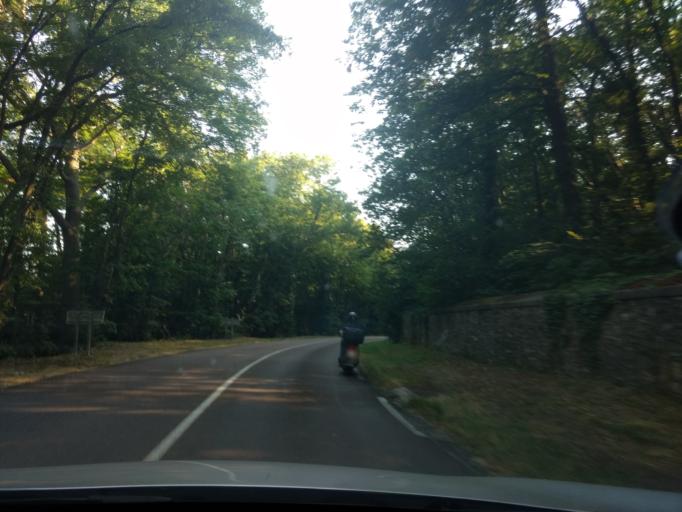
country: FR
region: Ile-de-France
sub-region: Departement de l'Essonne
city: Bievres
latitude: 48.7608
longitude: 2.2014
